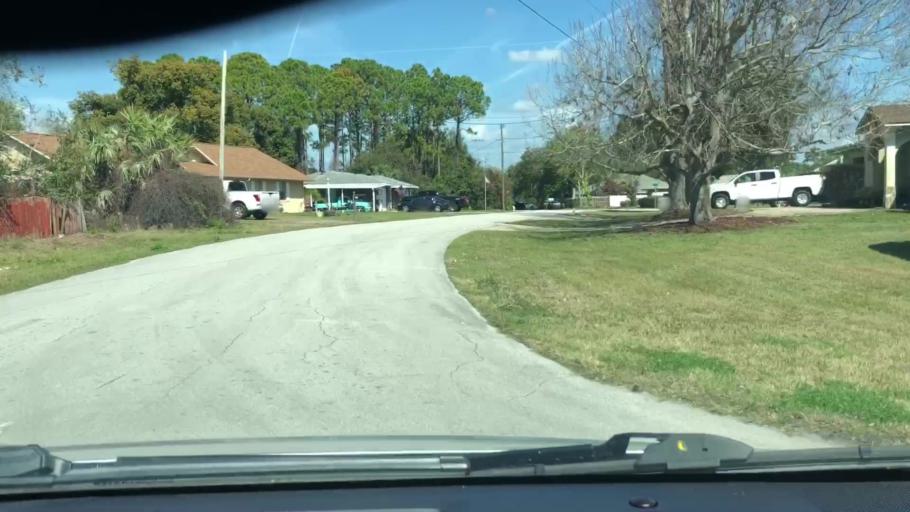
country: US
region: Florida
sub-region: Volusia County
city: Deltona
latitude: 28.8845
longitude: -81.2310
